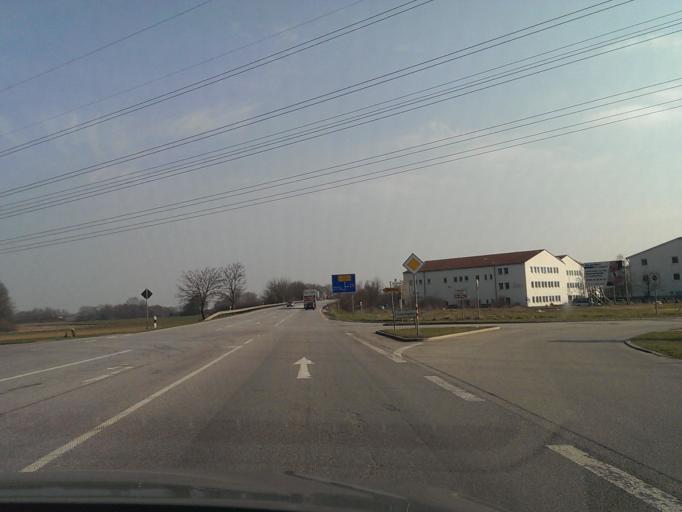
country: DE
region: Bavaria
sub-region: Upper Palatinate
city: Neutraubling
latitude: 48.9951
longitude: 12.2365
